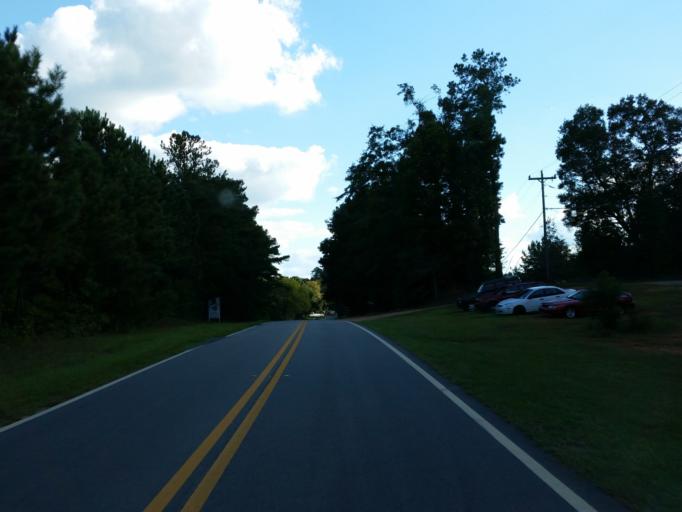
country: US
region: Georgia
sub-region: Butts County
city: Indian Springs
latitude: 33.1924
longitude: -84.0056
